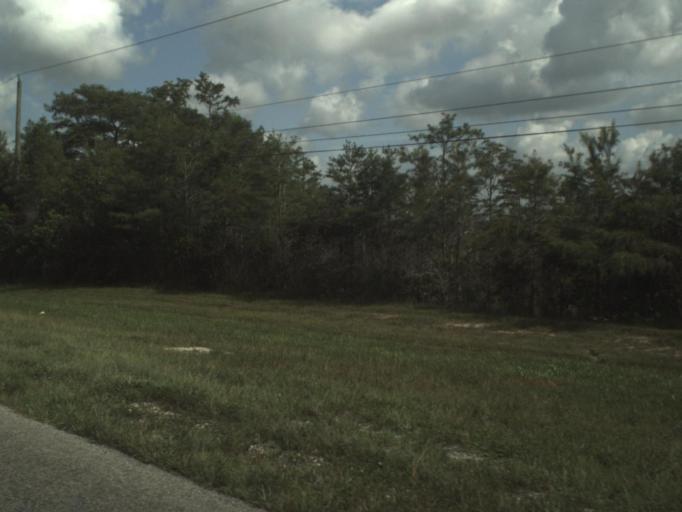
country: US
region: Florida
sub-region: Palm Beach County
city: Palm Beach Gardens
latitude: 26.8245
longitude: -80.1740
